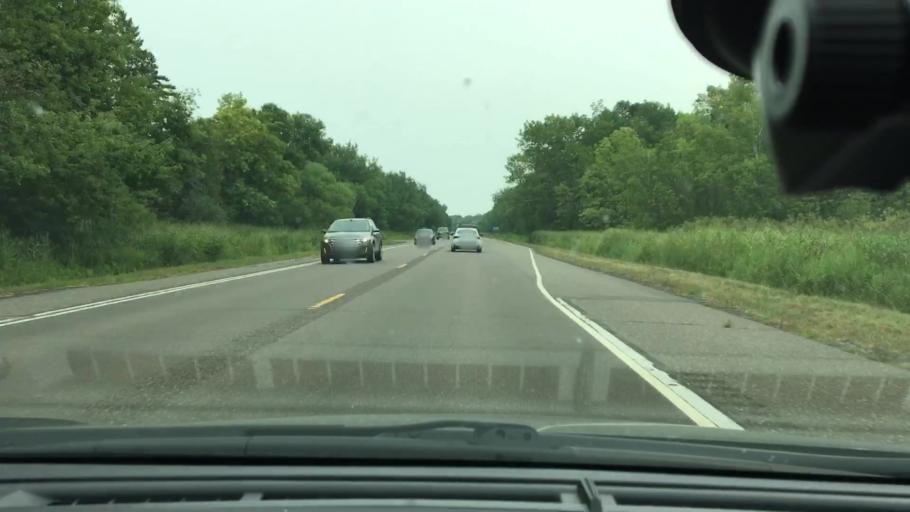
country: US
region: Minnesota
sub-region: Mille Lacs County
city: Vineland
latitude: 46.1519
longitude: -93.7457
